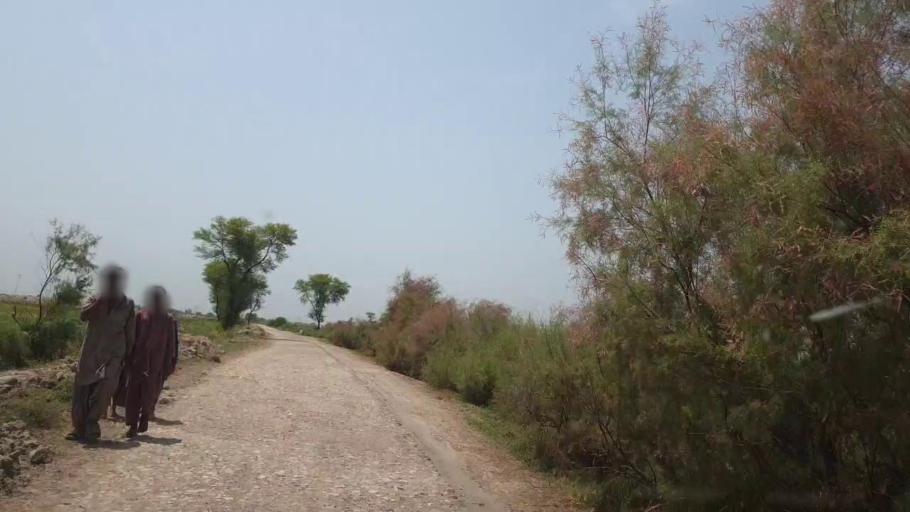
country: PK
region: Sindh
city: Shikarpur
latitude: 27.9073
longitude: 68.6335
